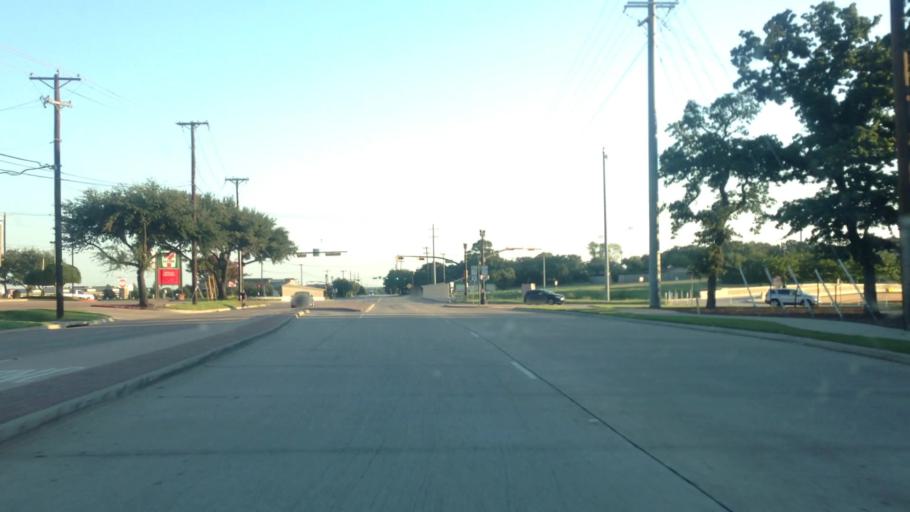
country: US
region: Texas
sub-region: Tarrant County
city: Southlake
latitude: 32.9499
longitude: -97.1341
